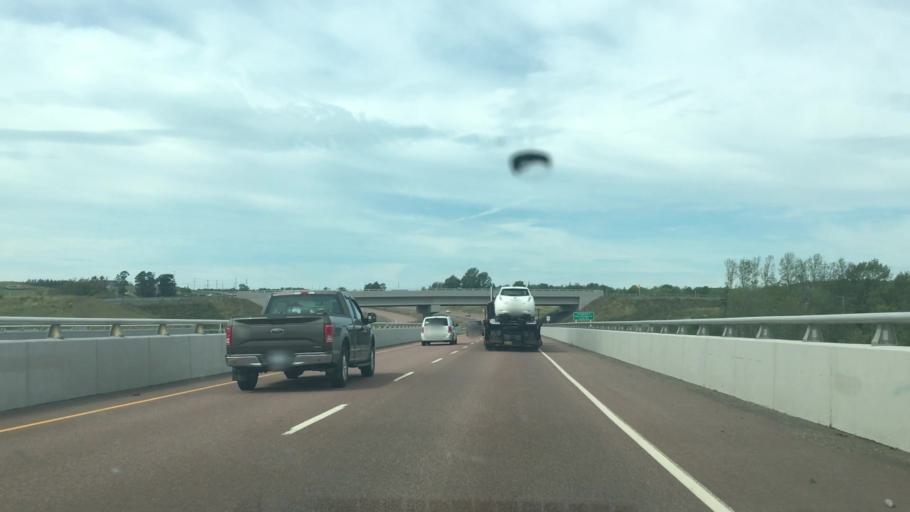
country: CA
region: Nova Scotia
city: Antigonish
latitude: 45.6030
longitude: -61.9163
